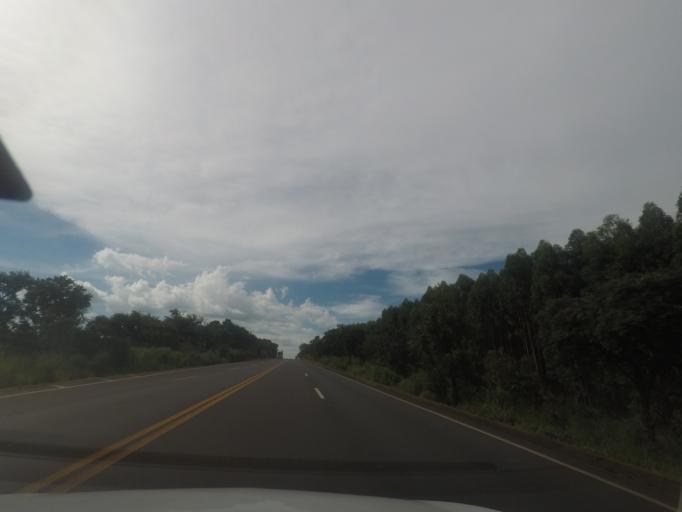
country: BR
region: Minas Gerais
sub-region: Prata
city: Prata
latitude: -19.1950
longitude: -48.9442
